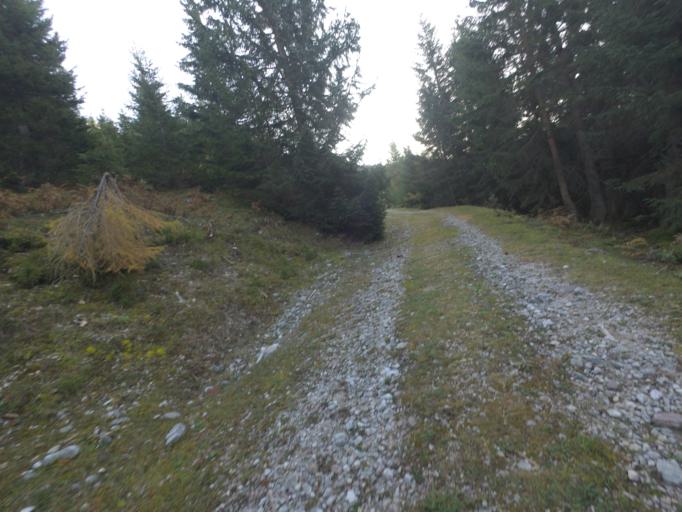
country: AT
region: Salzburg
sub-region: Politischer Bezirk Sankt Johann im Pongau
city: Werfenweng
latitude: 47.4849
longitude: 13.2295
